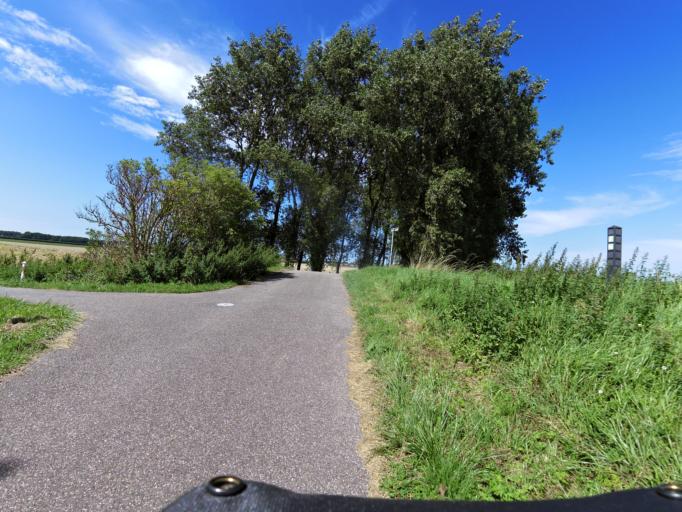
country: NL
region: Zeeland
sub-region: Gemeente Noord-Beveland
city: Kamperland
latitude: 51.5545
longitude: 3.7763
